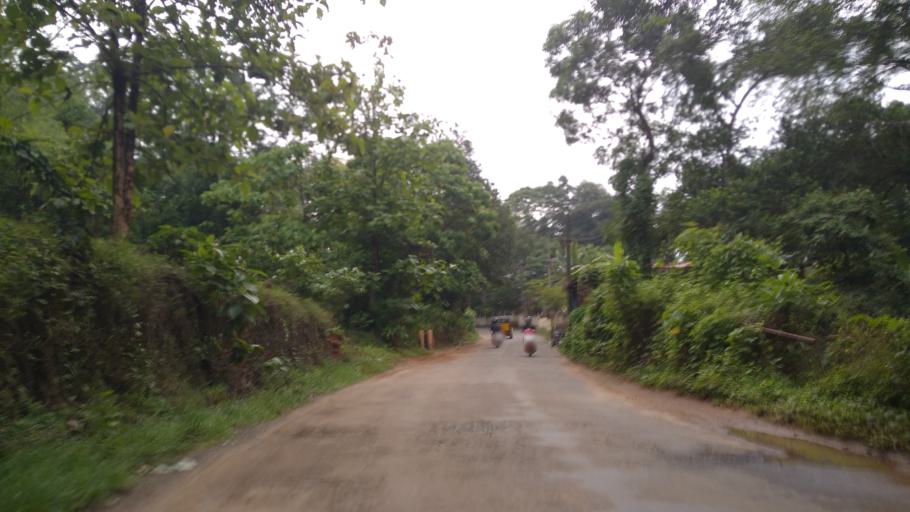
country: IN
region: Kerala
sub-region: Ernakulam
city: Perumpavur
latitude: 10.1212
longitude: 76.5539
